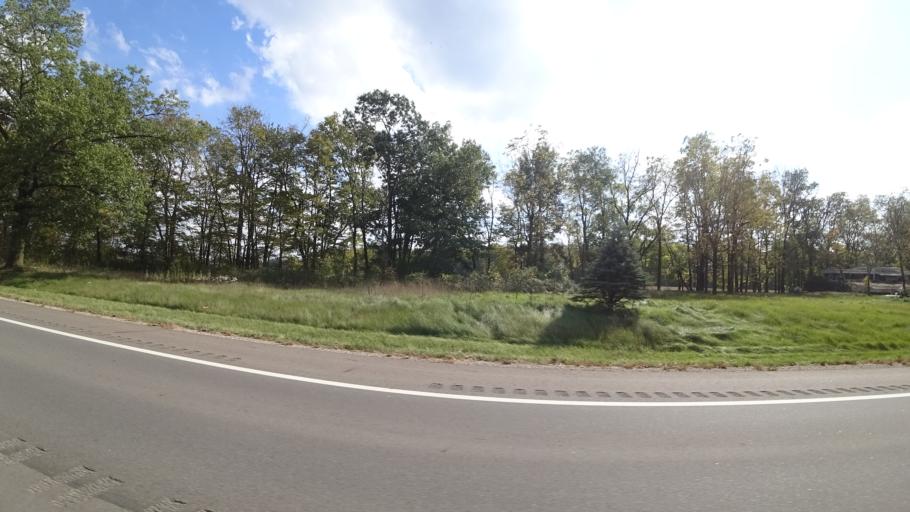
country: US
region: Michigan
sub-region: Calhoun County
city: Athens
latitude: 42.0624
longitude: -85.2039
